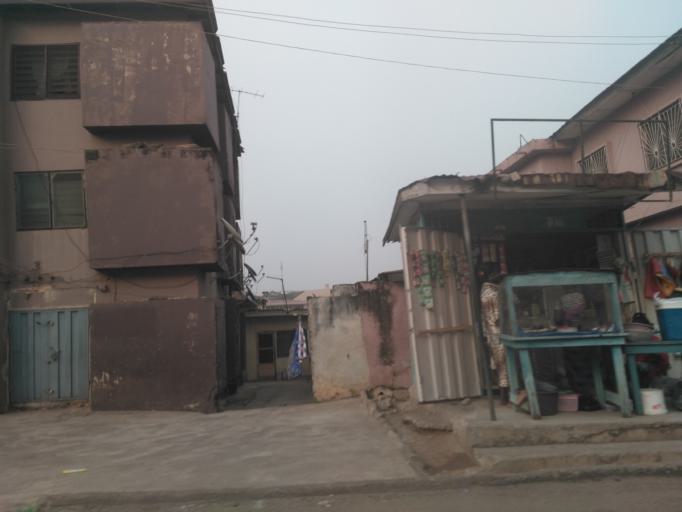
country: GH
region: Ashanti
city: Kumasi
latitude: 6.7087
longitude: -1.6189
